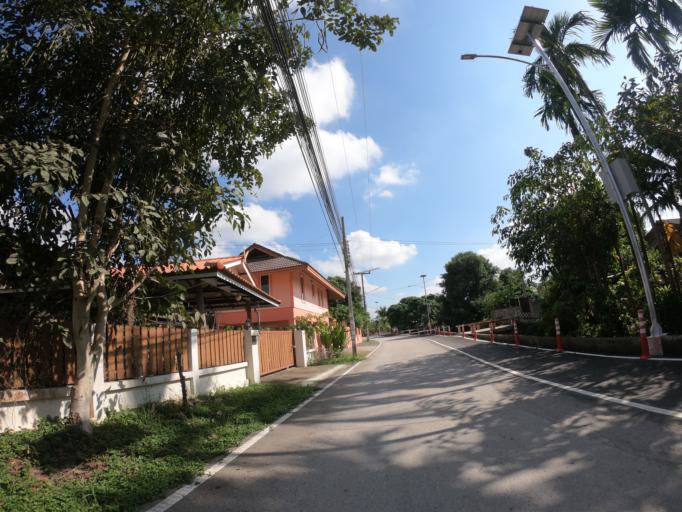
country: TH
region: Chiang Mai
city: San Sai
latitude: 18.8497
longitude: 99.0550
